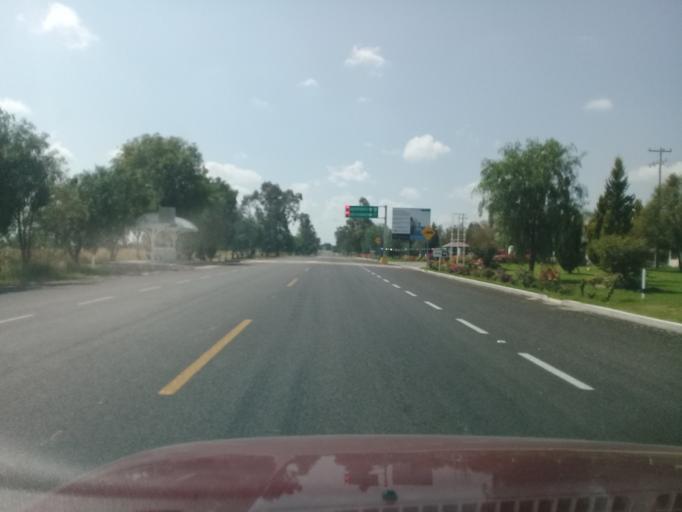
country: MX
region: Aguascalientes
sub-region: Aguascalientes
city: Penuelas (El Cienegal)
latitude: 21.7282
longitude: -102.3603
